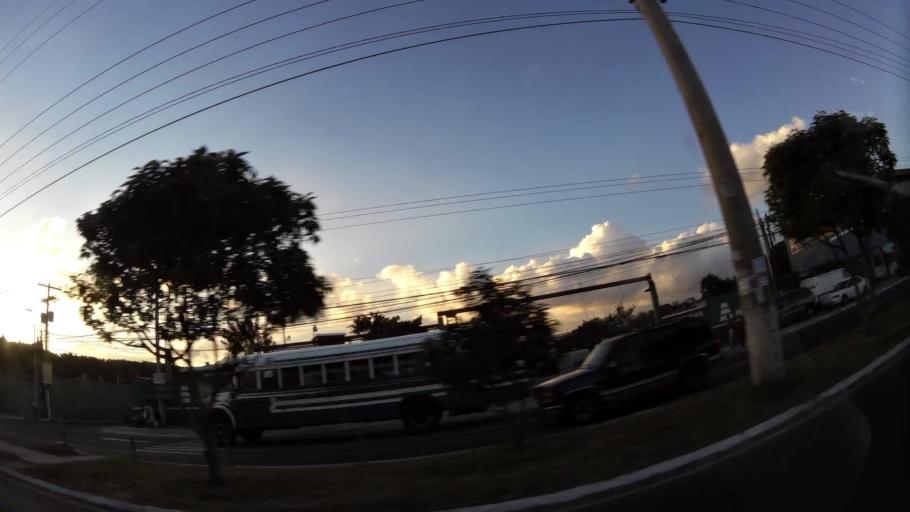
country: GT
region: Guatemala
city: Villa Nueva
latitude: 14.5109
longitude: -90.5802
